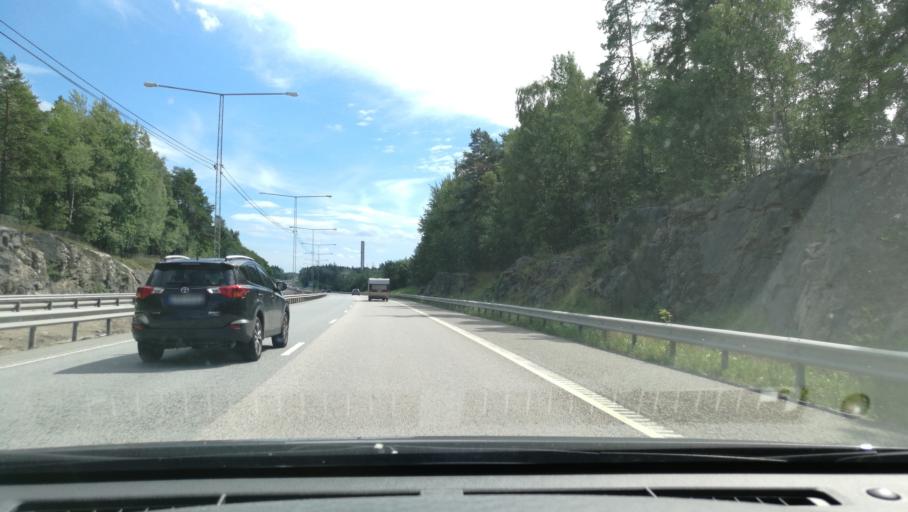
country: SE
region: Stockholm
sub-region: Jarfalla Kommun
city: Jakobsberg
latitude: 59.4364
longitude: 17.8440
